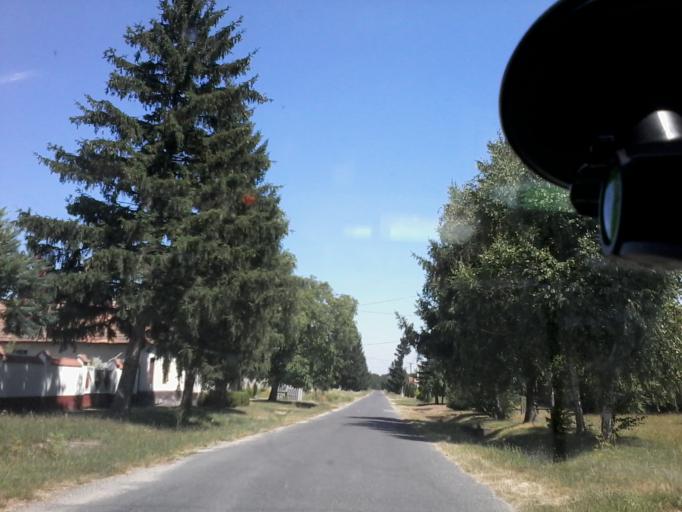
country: HU
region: Vas
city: Celldomolk
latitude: 47.1930
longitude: 17.1120
